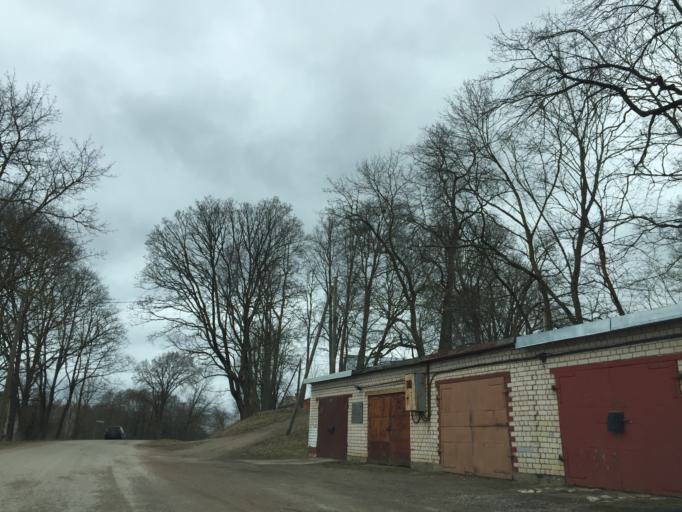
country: LV
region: Ilukste
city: Ilukste
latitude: 55.9039
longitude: 26.3746
